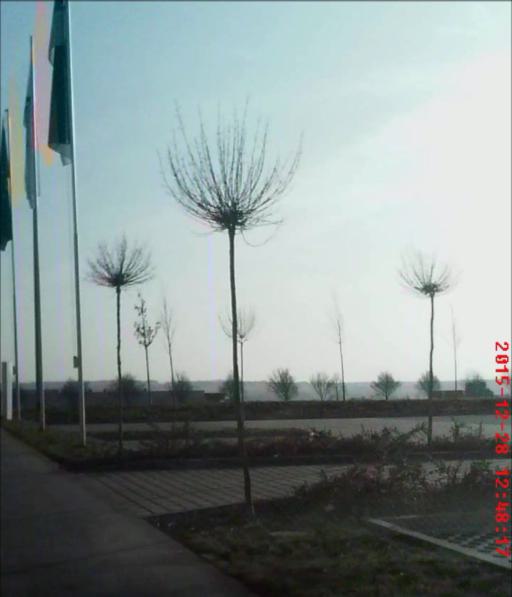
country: DE
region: Thuringia
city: Niederrossla
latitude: 51.0135
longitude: 11.4649
